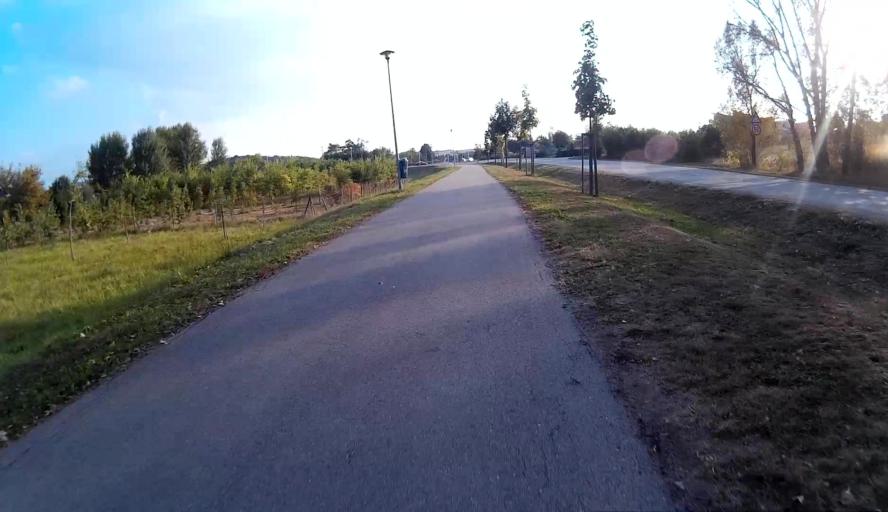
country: CZ
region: South Moravian
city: Podoli
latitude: 49.1845
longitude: 16.7231
